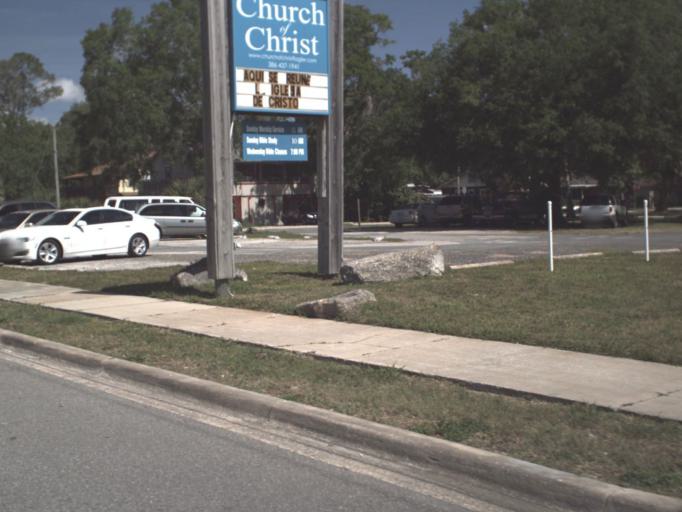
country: US
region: Florida
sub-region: Flagler County
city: Bunnell
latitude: 29.4679
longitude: -81.2606
